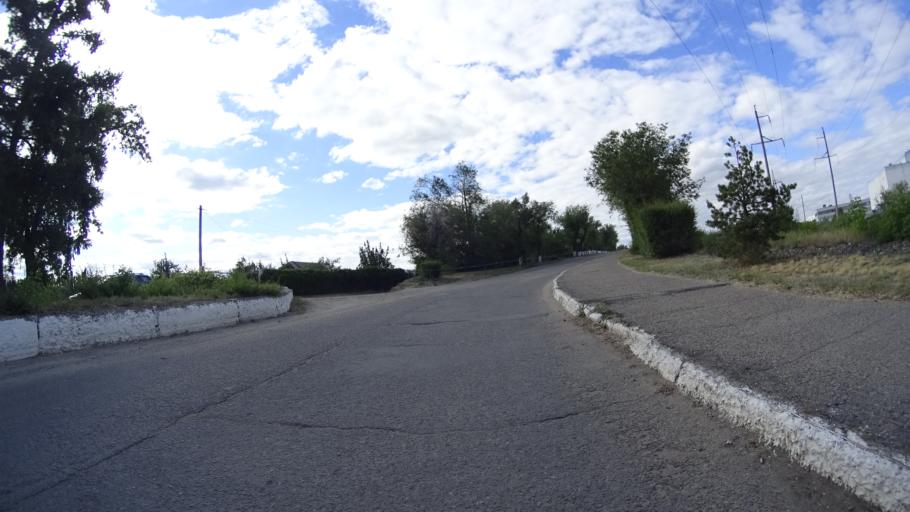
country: RU
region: Chelyabinsk
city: Troitsk
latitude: 54.0378
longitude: 61.6400
